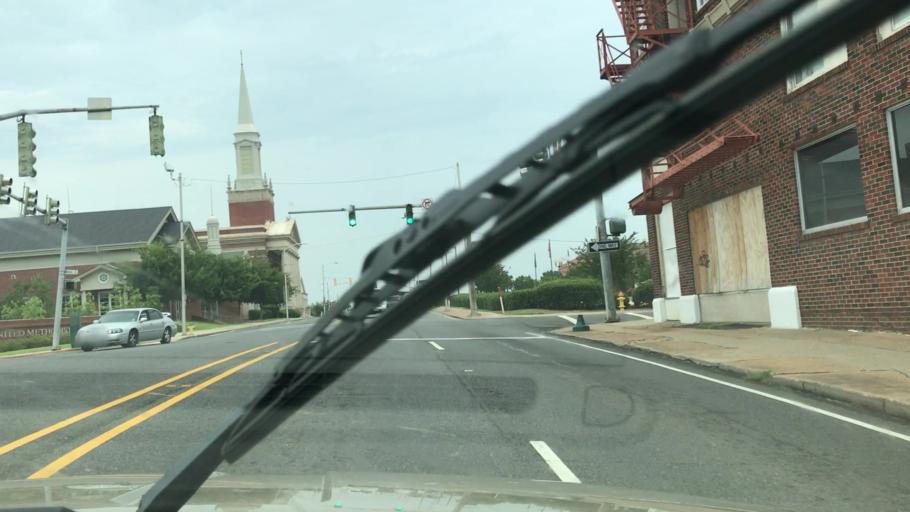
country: US
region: Louisiana
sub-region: Caddo Parish
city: Shreveport
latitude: 32.5097
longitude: -93.7515
